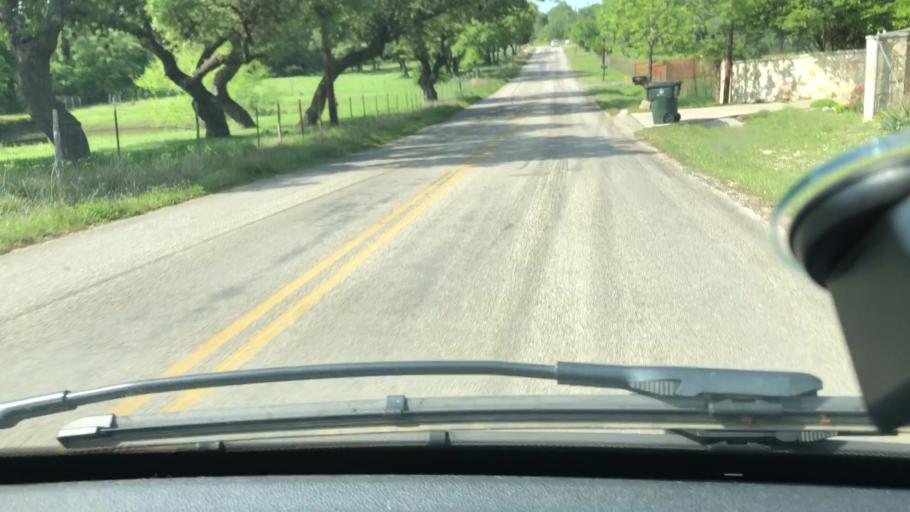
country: US
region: Texas
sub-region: Comal County
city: Bulverde
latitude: 29.7729
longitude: -98.4588
